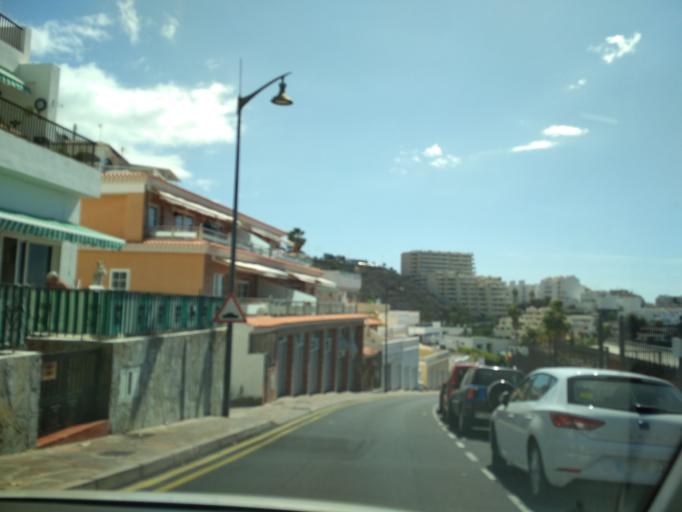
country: ES
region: Canary Islands
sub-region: Provincia de Santa Cruz de Tenerife
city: Santiago del Teide
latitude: 28.2444
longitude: -16.8390
